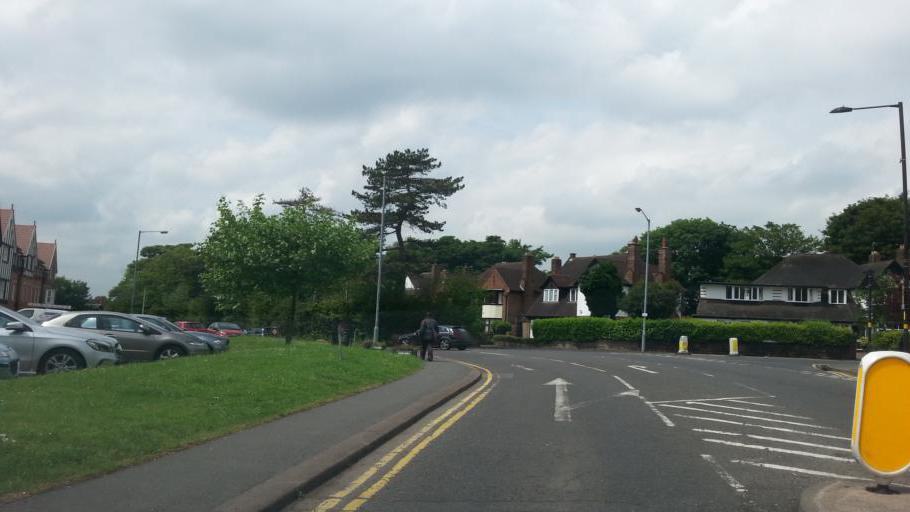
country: GB
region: England
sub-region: City and Borough of Birmingham
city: Birmingham
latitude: 52.4459
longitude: -1.8838
